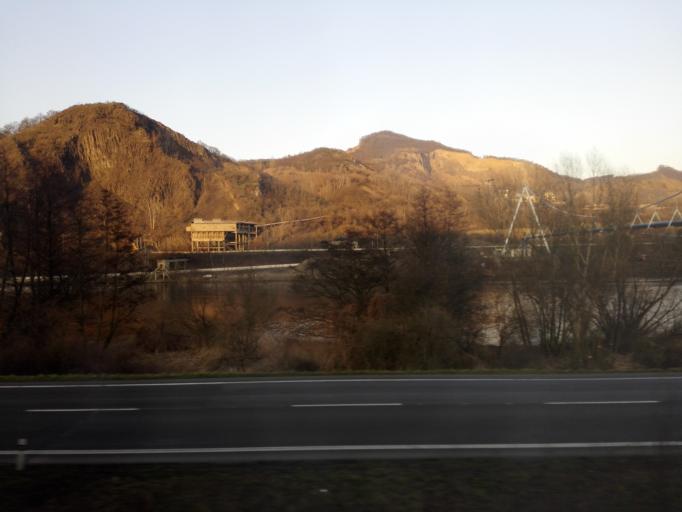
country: CZ
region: Ustecky
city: Lovosice
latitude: 50.5798
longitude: 14.0338
